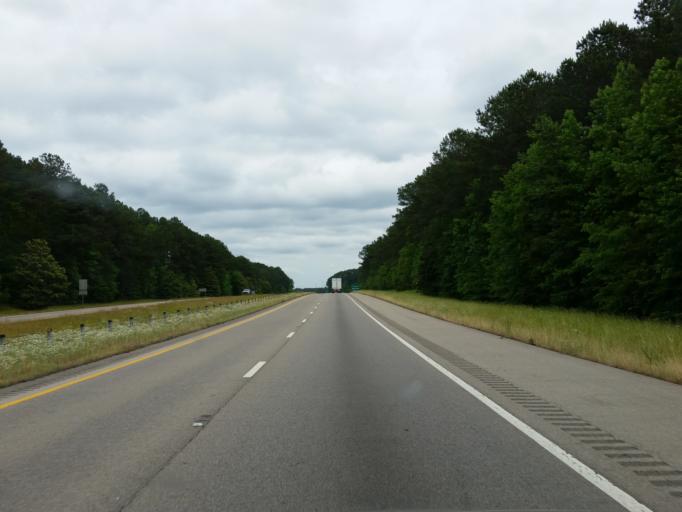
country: US
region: Alabama
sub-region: Sumter County
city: York
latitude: 32.4472
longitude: -88.4090
